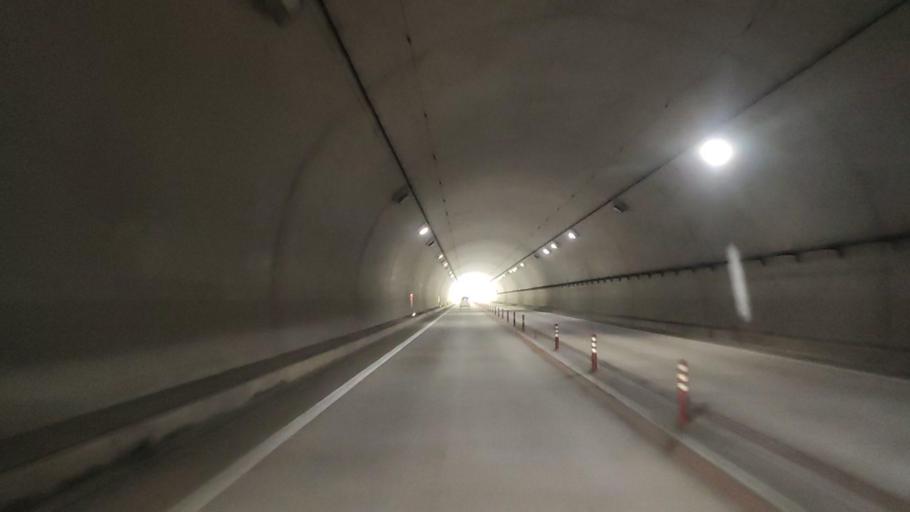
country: JP
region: Wakayama
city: Shingu
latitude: 33.6234
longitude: 135.9195
